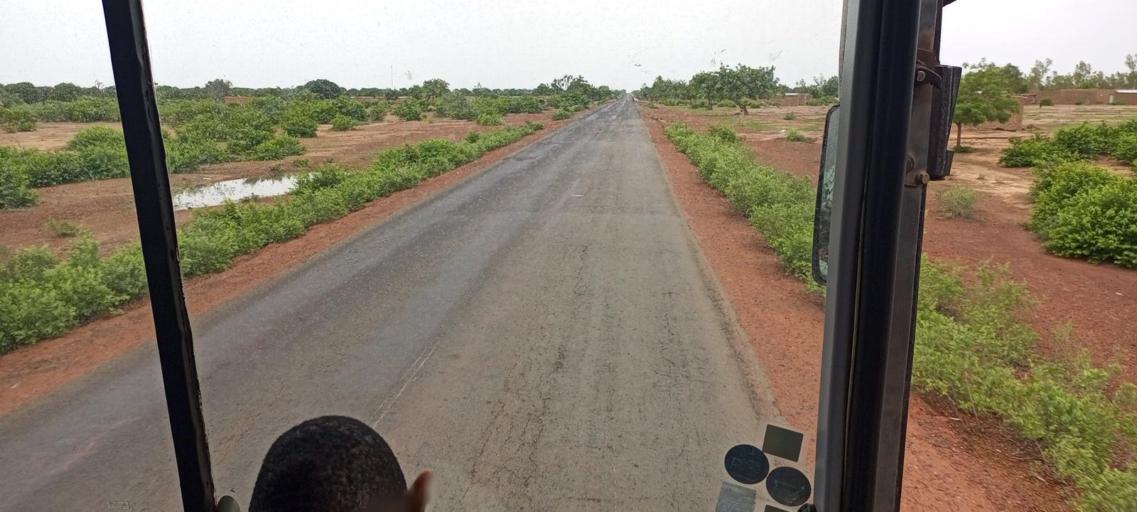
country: ML
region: Sikasso
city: Koutiala
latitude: 12.5478
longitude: -5.5818
